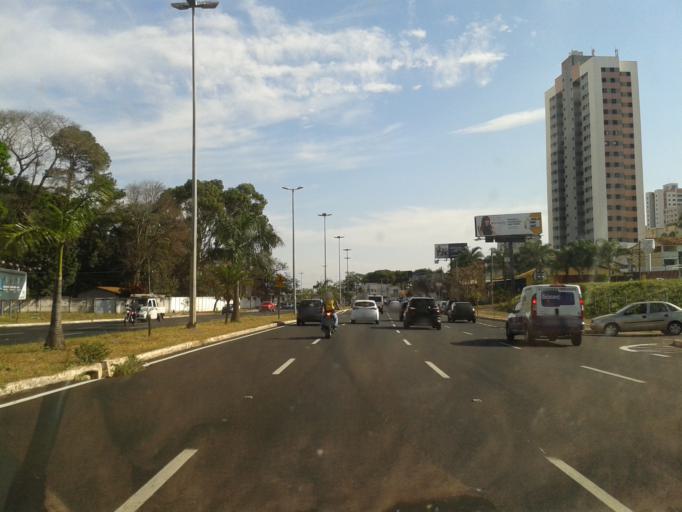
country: BR
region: Minas Gerais
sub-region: Uberlandia
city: Uberlandia
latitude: -18.9216
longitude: -48.2694
